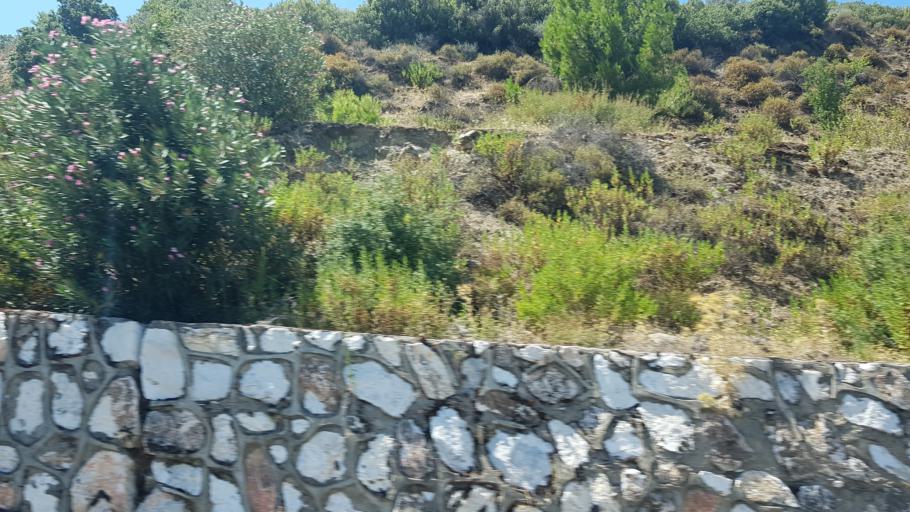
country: TR
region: Aydin
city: Akcaova
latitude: 37.5114
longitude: 28.0979
